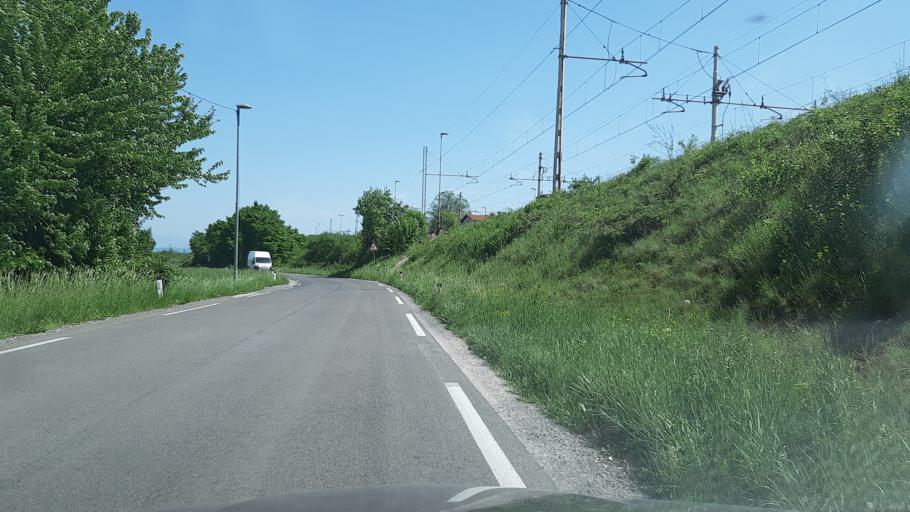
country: SI
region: Brezovica
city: Notranje Gorice
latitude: 45.9647
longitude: 14.3947
